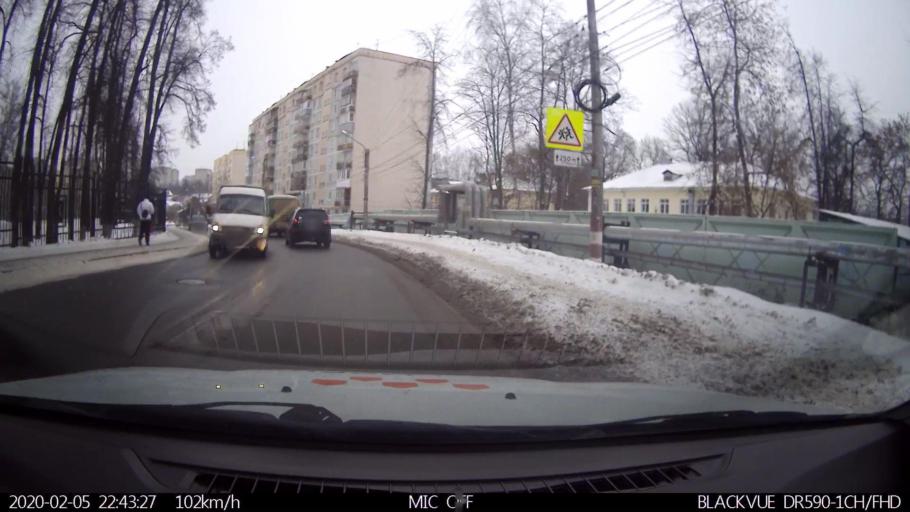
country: RU
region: Nizjnij Novgorod
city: Imeni Stepana Razina
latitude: 54.7123
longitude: 44.3776
